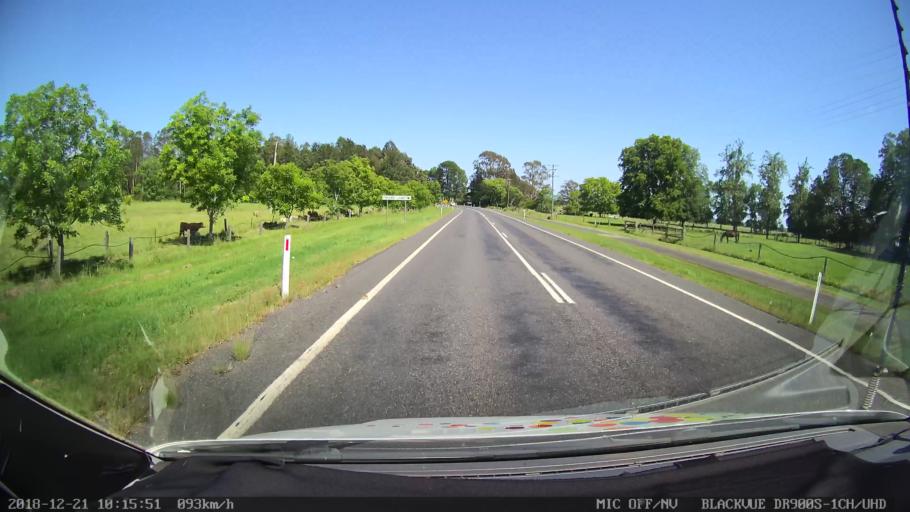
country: AU
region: New South Wales
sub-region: Clarence Valley
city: South Grafton
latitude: -29.6871
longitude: 152.8938
